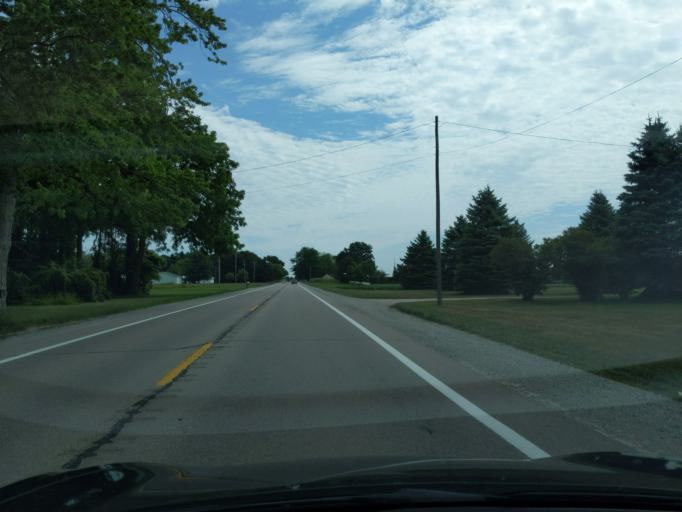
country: US
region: Michigan
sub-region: Gratiot County
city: Breckenridge
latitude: 43.4080
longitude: -84.4218
